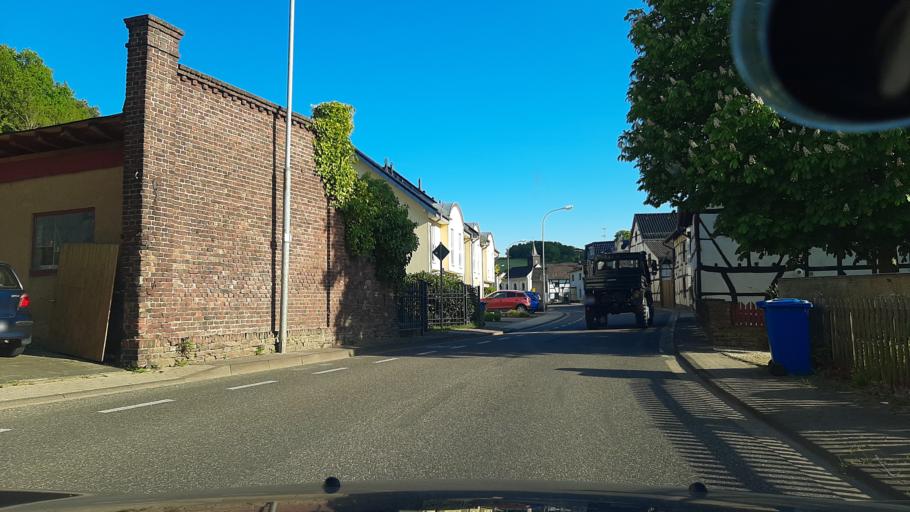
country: DE
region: North Rhine-Westphalia
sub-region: Regierungsbezirk Koln
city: Mechernich
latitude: 50.5811
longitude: 6.6753
